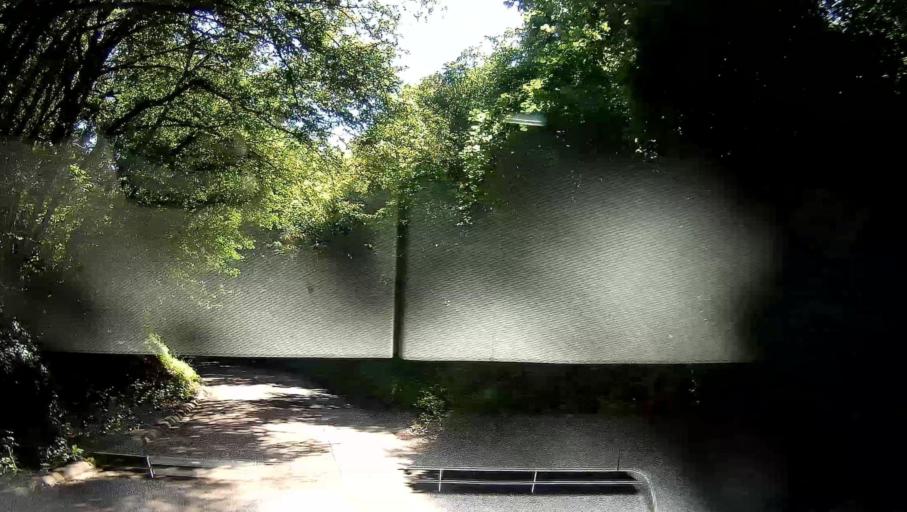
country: FR
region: Bourgogne
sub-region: Departement de la Cote-d'Or
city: Nolay
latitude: 46.9775
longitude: 4.6579
